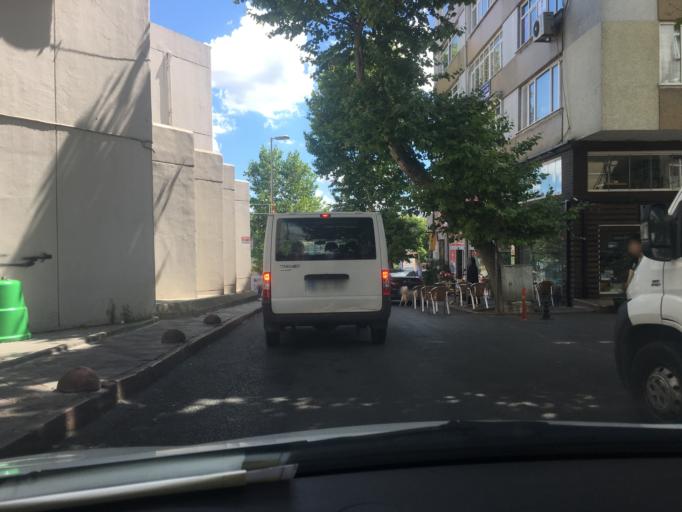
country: TR
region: Istanbul
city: Istanbul
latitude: 41.0091
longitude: 28.9484
